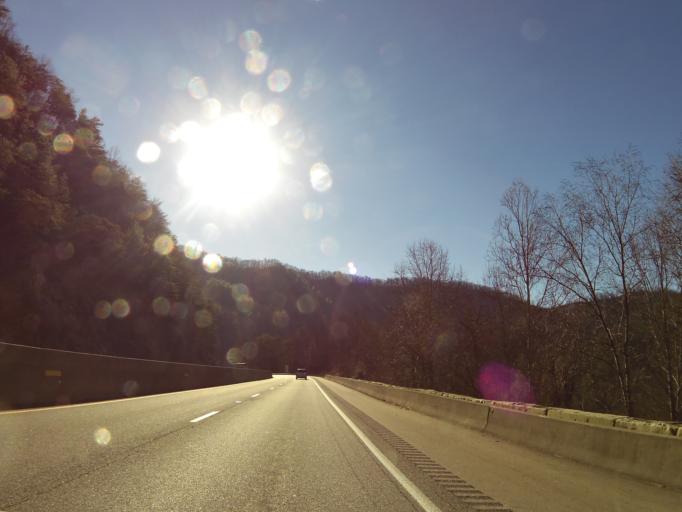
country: US
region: North Carolina
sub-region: Haywood County
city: Cove Creek
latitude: 35.7119
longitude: -83.0310
